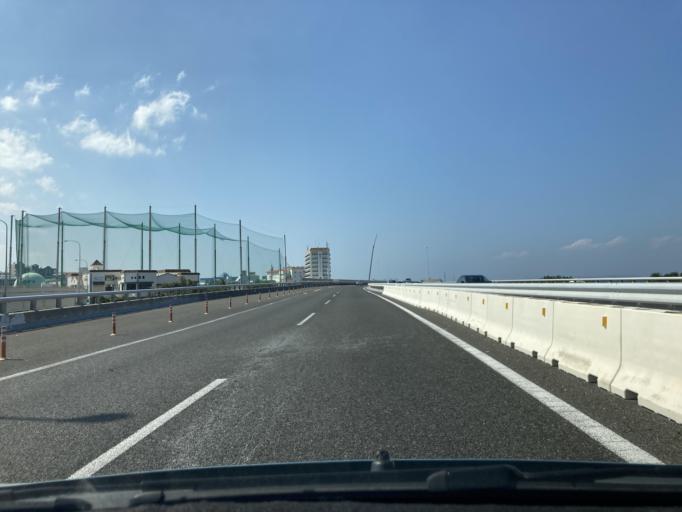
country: JP
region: Okinawa
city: Naha-shi
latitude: 26.2216
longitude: 127.6704
